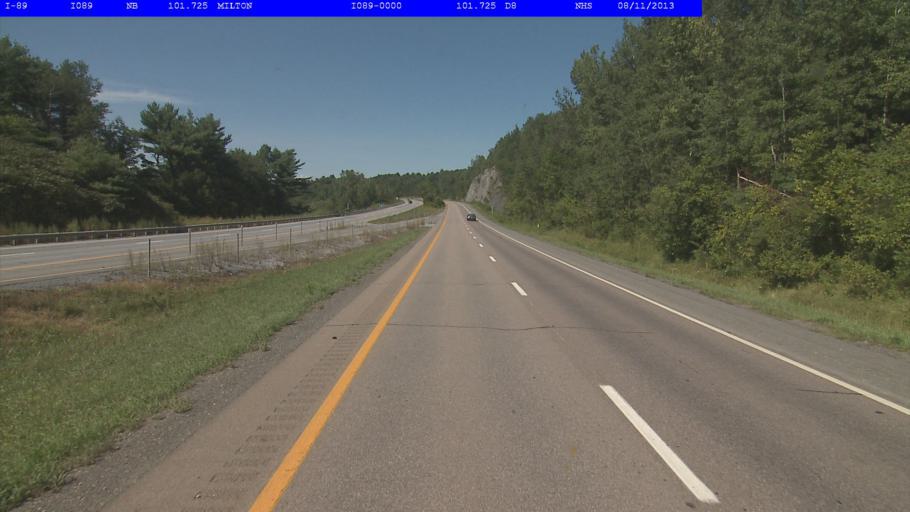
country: US
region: Vermont
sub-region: Chittenden County
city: Milton
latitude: 44.6383
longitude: -73.1402
